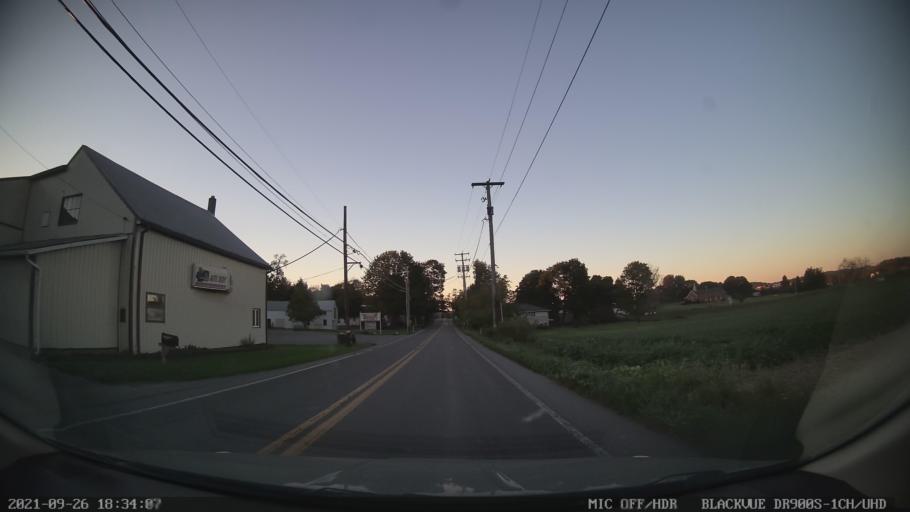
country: US
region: Pennsylvania
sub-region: Berks County
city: Kutztown
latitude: 40.5076
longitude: -75.7705
